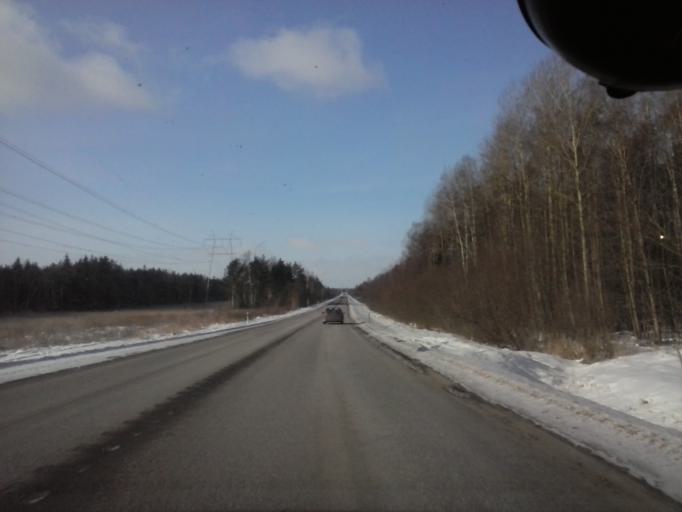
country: EE
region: Tartu
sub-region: Noo vald
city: Noo
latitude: 58.3452
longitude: 26.4852
